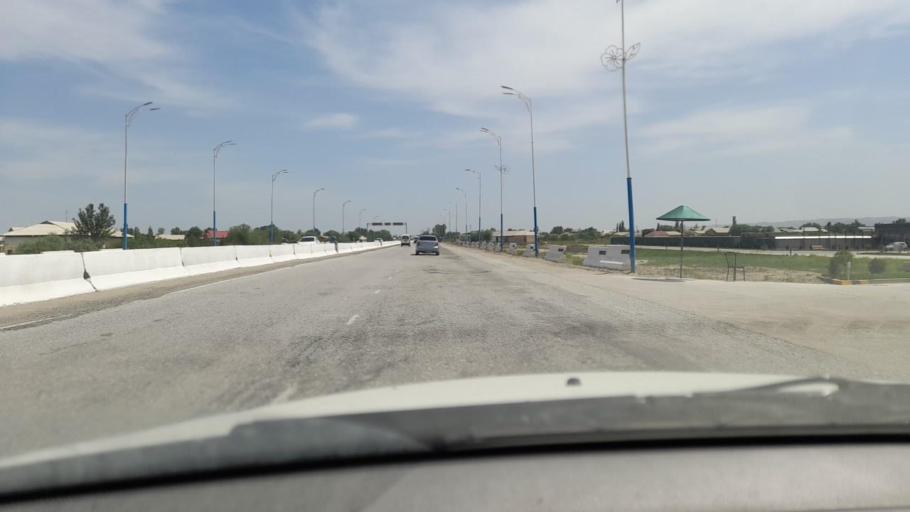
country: UZ
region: Navoiy
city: Navoiy
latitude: 40.1174
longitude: 65.4923
